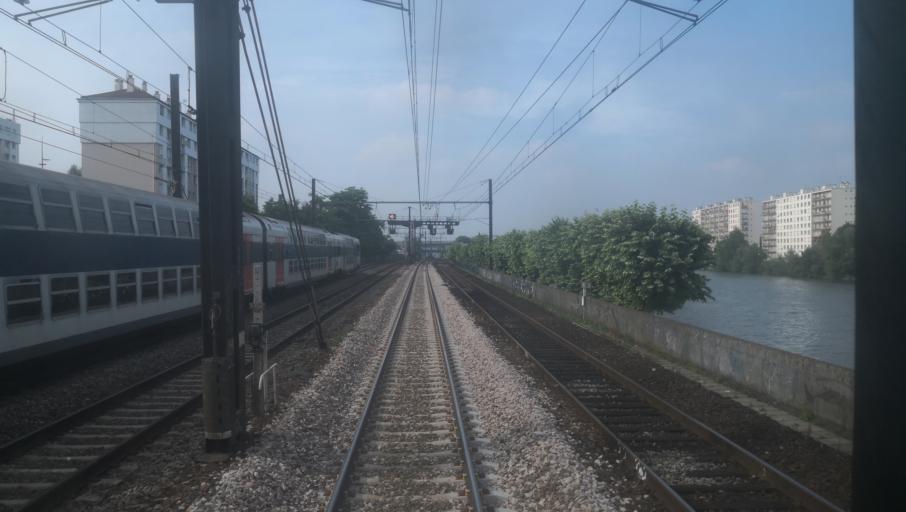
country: FR
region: Ile-de-France
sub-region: Departement du Val-de-Marne
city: Choisy-le-Roi
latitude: 48.7682
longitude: 2.4109
